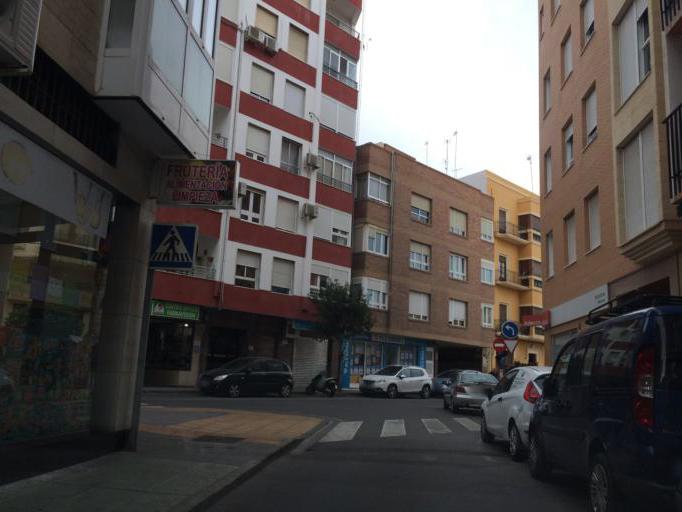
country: ES
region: Andalusia
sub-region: Provincia de Almeria
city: Almeria
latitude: 36.8424
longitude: -2.4594
